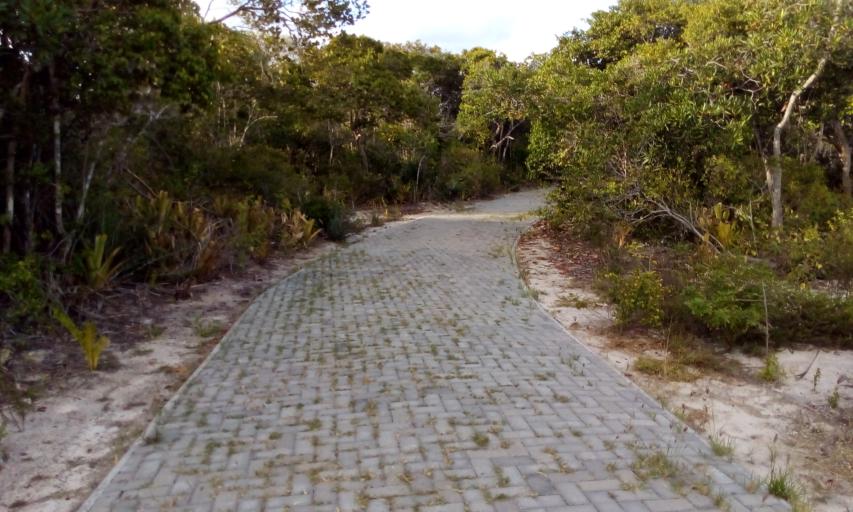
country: BR
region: Bahia
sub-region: Mata De Sao Joao
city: Mata de Sao Joao
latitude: -12.5667
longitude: -38.0047
